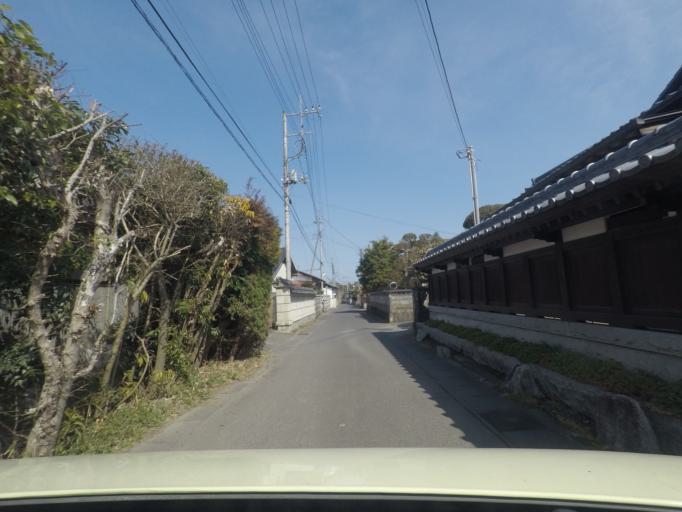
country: JP
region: Ibaraki
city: Ishioka
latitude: 36.1984
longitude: 140.3145
